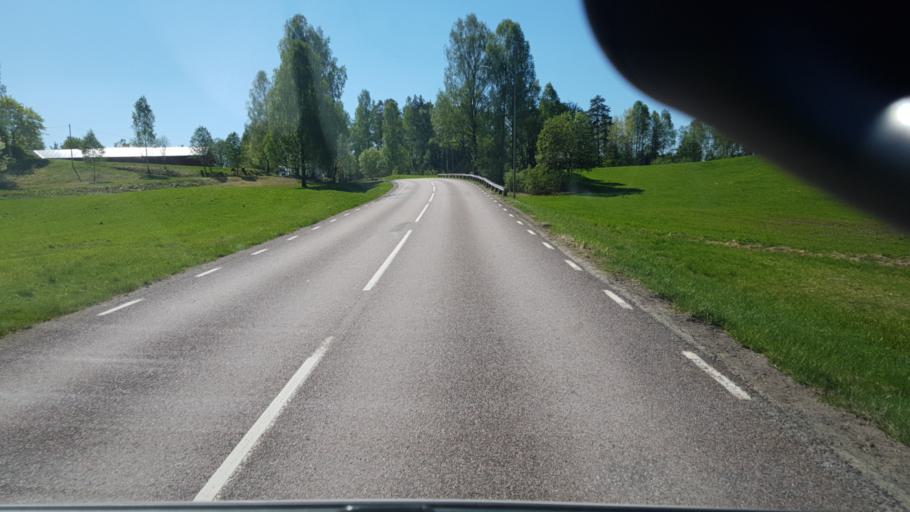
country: SE
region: Vaermland
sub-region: Arvika Kommun
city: Arvika
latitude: 59.8504
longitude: 12.5484
